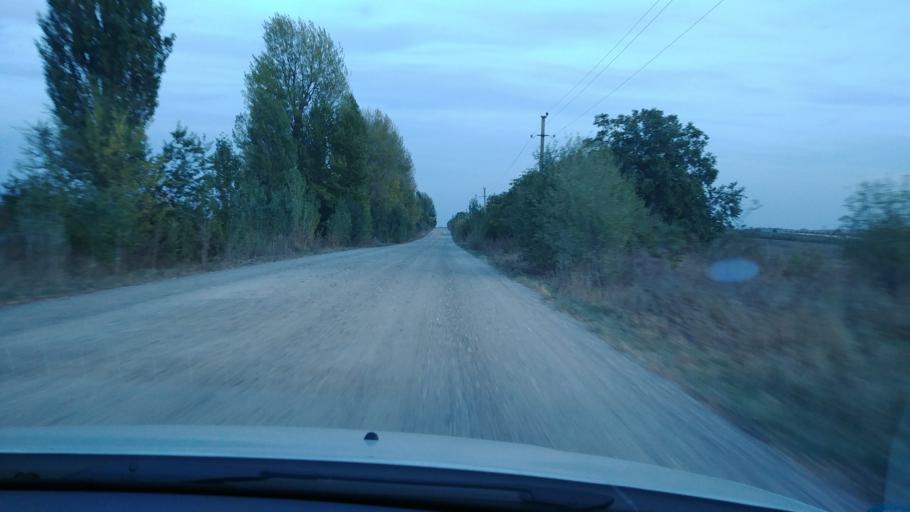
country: MD
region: Rezina
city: Saharna
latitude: 47.6725
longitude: 28.9380
